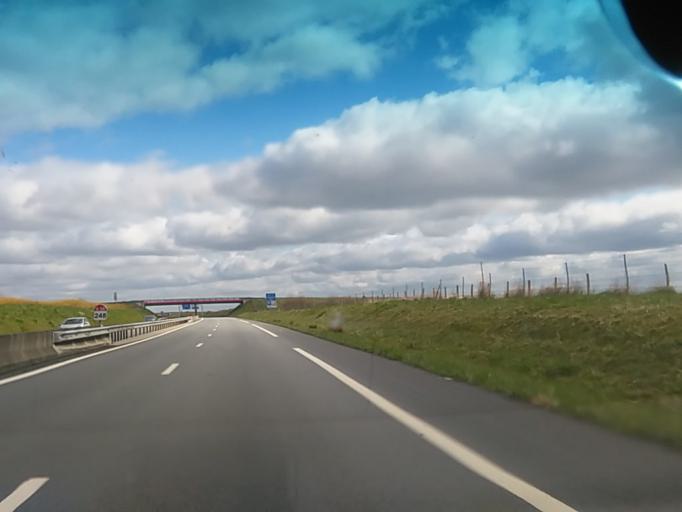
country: FR
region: Haute-Normandie
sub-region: Departement de l'Eure
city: Bernay
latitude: 49.1398
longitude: 0.5690
